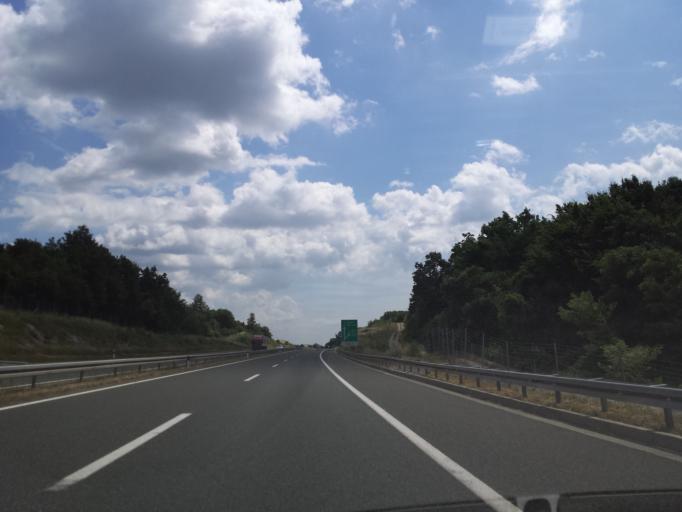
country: HR
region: Karlovacka
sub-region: Grad Ogulin
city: Ogulin
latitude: 45.4003
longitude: 15.2233
